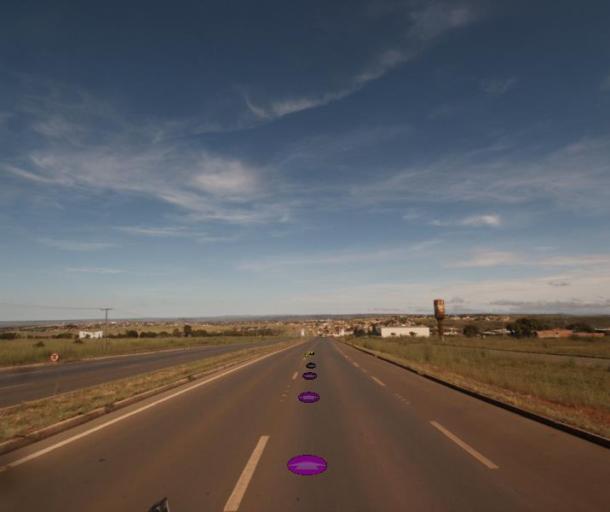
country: BR
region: Federal District
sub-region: Brasilia
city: Brasilia
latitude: -15.7386
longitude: -48.2991
